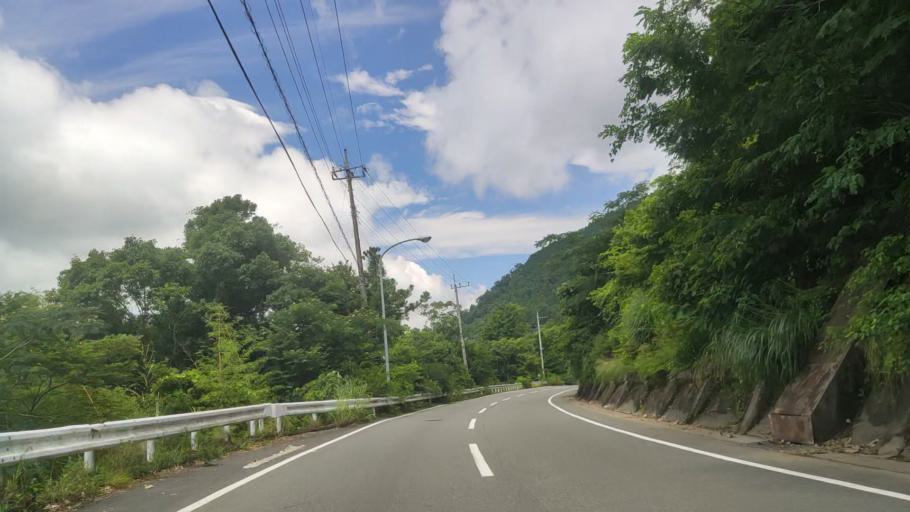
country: JP
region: Shizuoka
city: Fujinomiya
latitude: 35.2496
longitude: 138.4873
